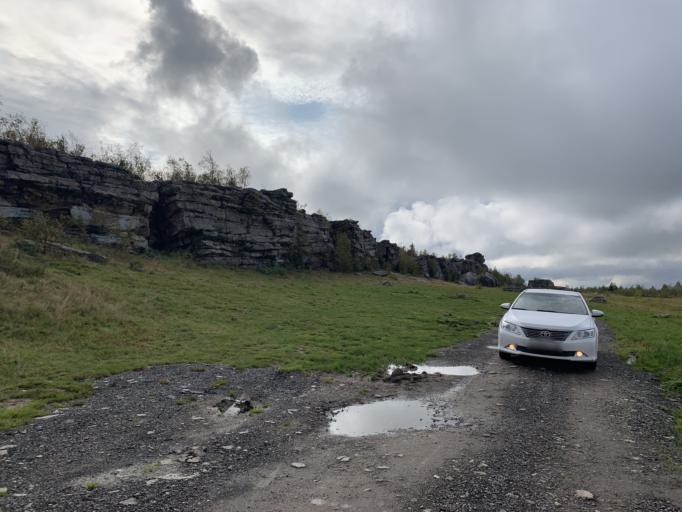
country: RU
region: Perm
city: Gubakha
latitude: 58.8326
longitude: 57.5846
